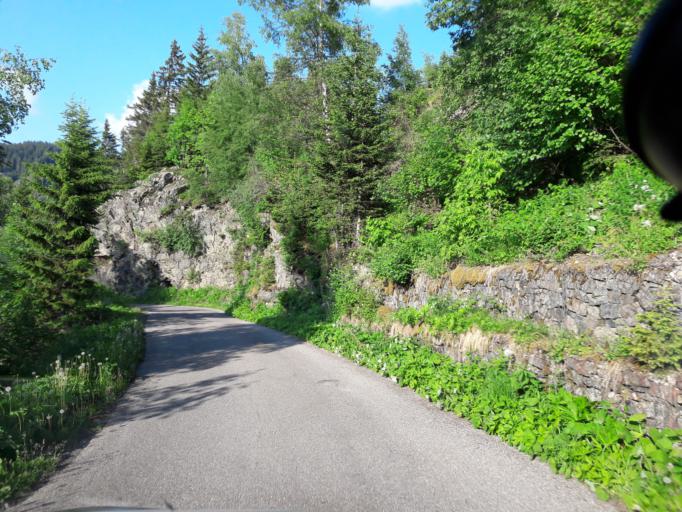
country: FR
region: Rhone-Alpes
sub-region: Departement de l'Isere
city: Livet-et-Gavet
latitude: 45.0522
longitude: 5.8859
